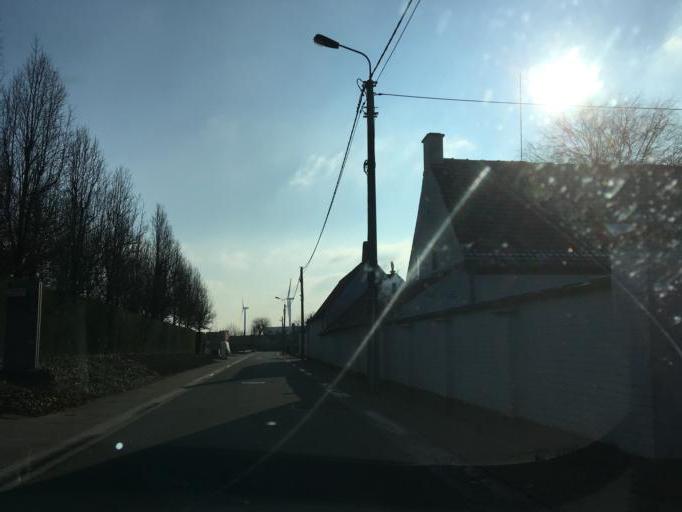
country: BE
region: Flanders
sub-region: Provincie West-Vlaanderen
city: Roeselare
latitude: 50.9501
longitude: 3.1581
